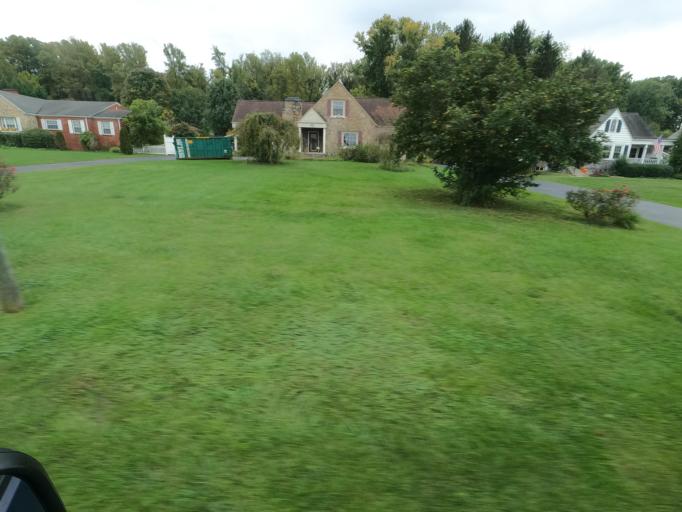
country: US
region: Tennessee
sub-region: Carter County
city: Central
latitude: 36.3401
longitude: -82.2526
